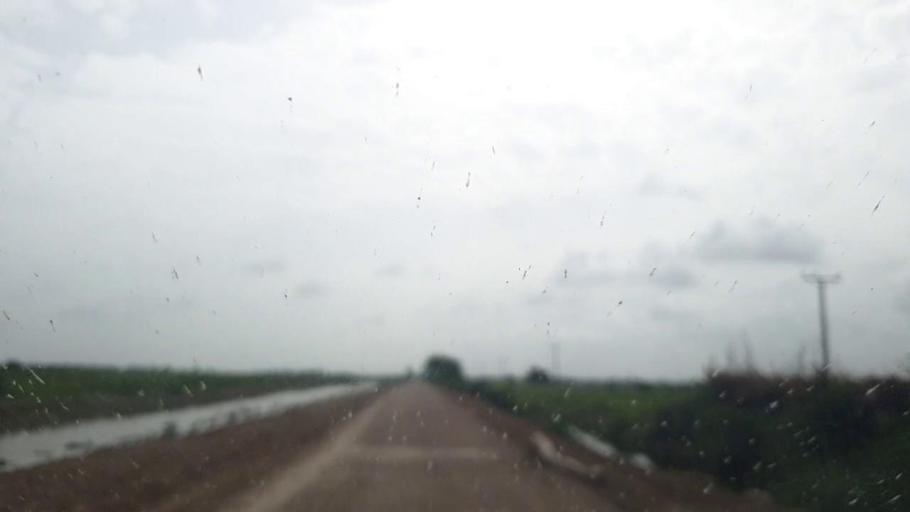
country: PK
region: Sindh
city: Tando Bago
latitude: 24.7991
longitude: 68.9998
